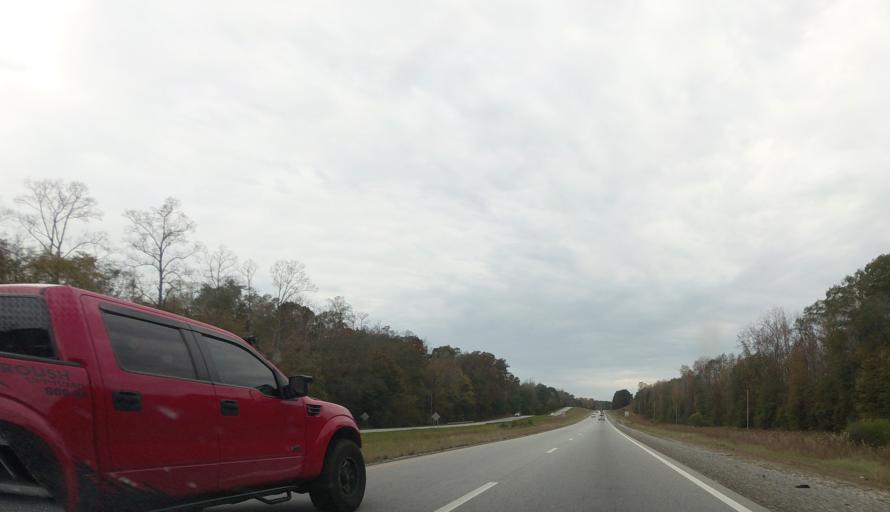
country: US
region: Alabama
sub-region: Lee County
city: Opelika
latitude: 32.6355
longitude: -85.2941
